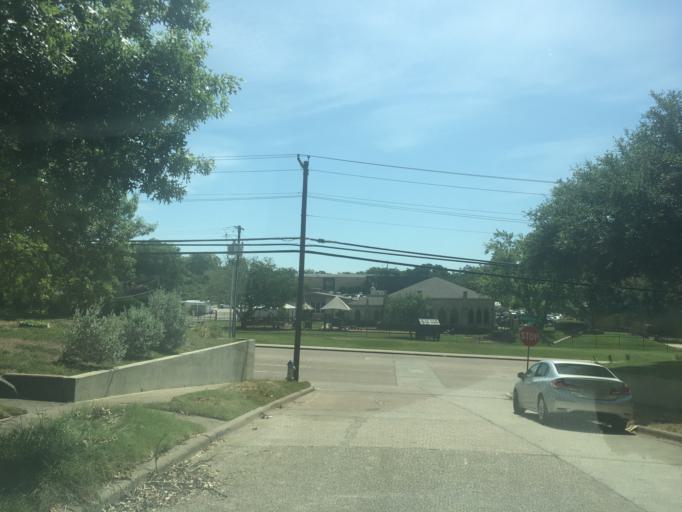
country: US
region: Texas
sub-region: Dallas County
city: Richardson
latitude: 32.8721
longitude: -96.7185
